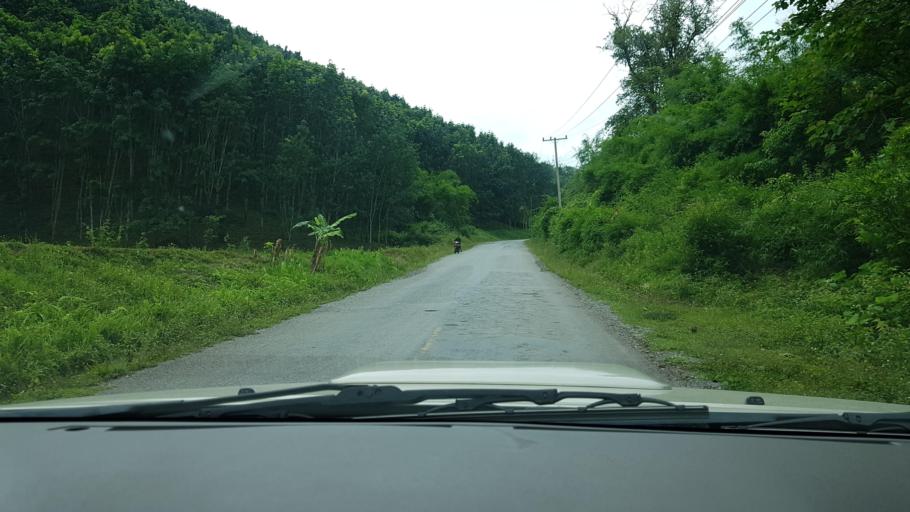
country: LA
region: Loungnamtha
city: Muang Nale
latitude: 20.3627
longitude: 101.7122
